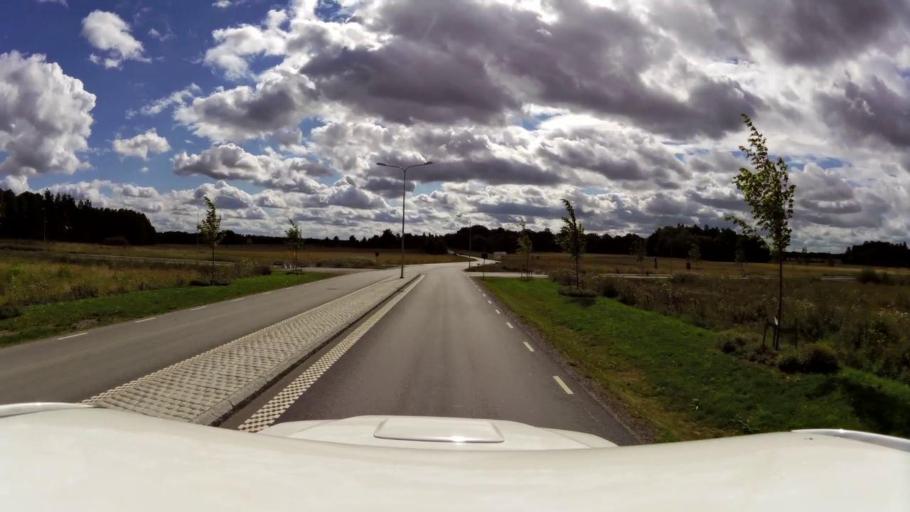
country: SE
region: OEstergoetland
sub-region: Linkopings Kommun
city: Linkoping
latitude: 58.3856
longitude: 15.5922
